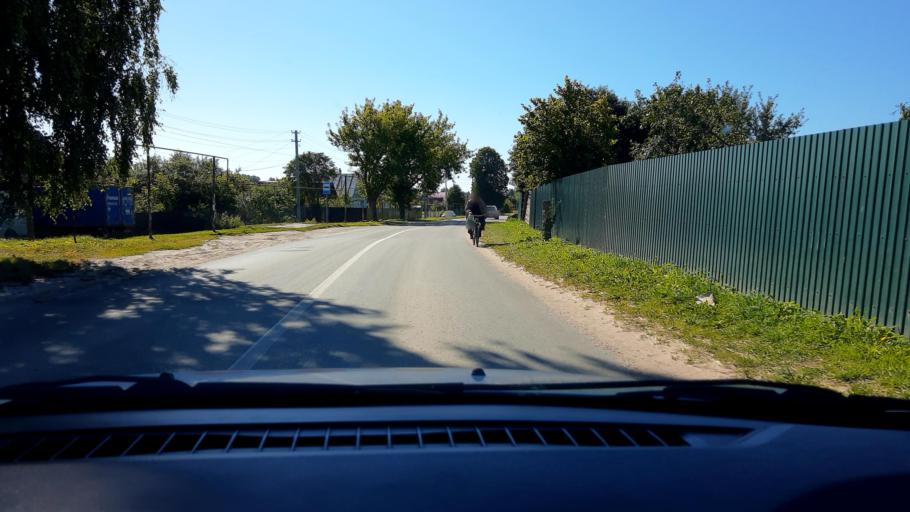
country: RU
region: Nizjnij Novgorod
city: Zavolzh'ye
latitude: 56.7229
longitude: 43.4137
